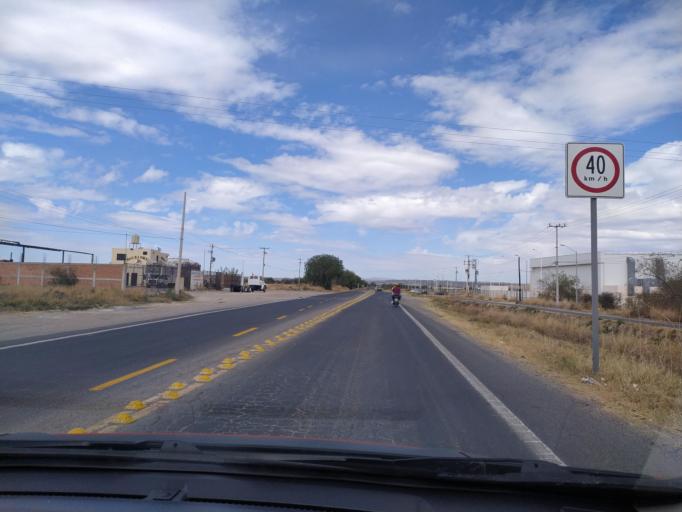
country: LA
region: Oudomxai
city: Muang La
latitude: 21.0017
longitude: 101.8319
